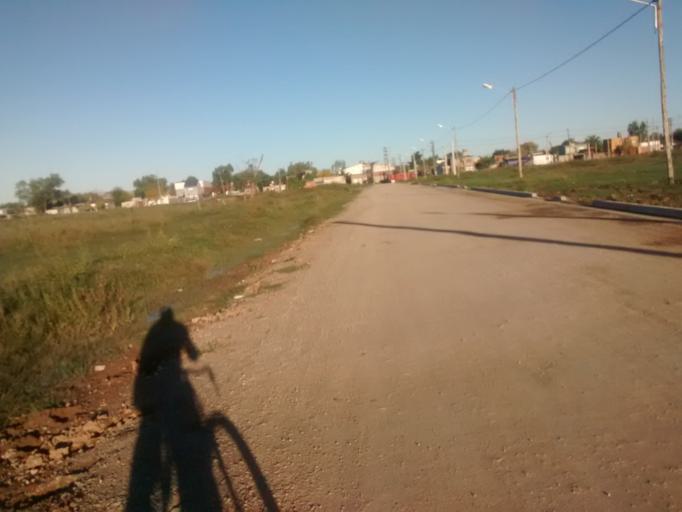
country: AR
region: Buenos Aires
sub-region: Partido de La Plata
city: La Plata
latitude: -34.9026
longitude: -57.9185
